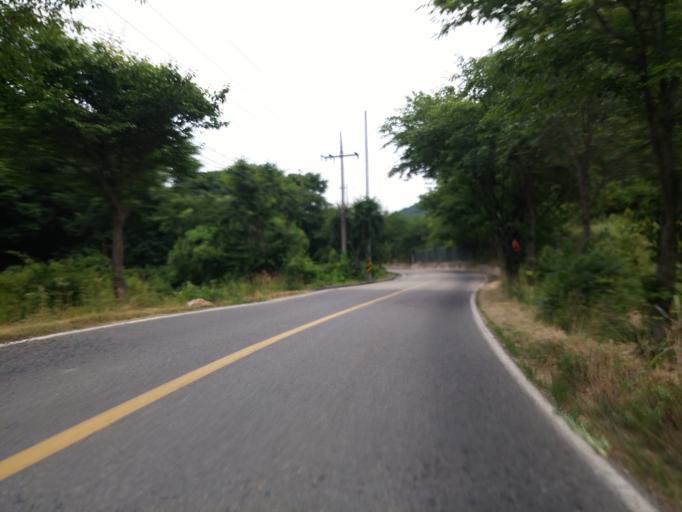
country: KR
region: Chungcheongnam-do
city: Kinzan
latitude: 36.1894
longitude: 127.5463
